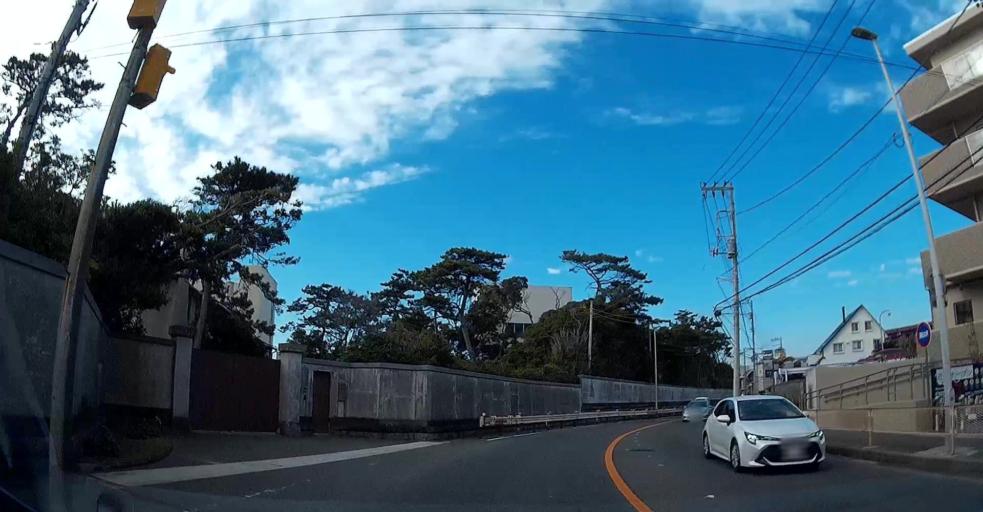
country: JP
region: Kanagawa
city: Hayama
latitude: 35.2668
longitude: 139.5707
